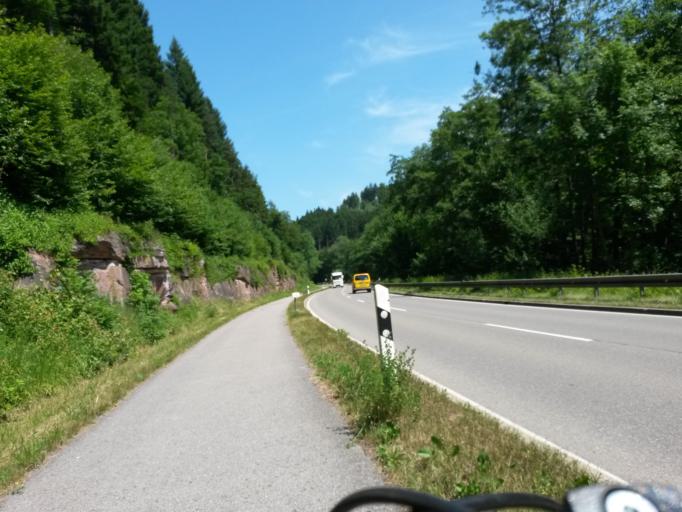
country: DE
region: Baden-Wuerttemberg
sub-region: Karlsruhe Region
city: Calw
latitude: 48.6990
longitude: 8.7393
